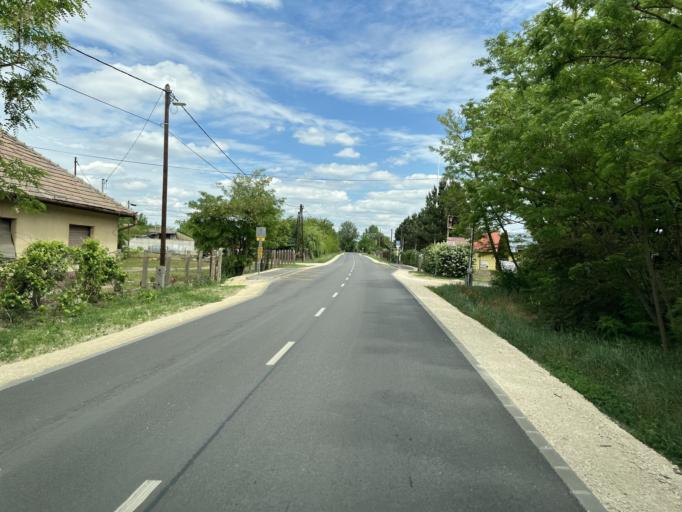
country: HU
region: Pest
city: Koka
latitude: 47.4733
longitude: 19.5631
